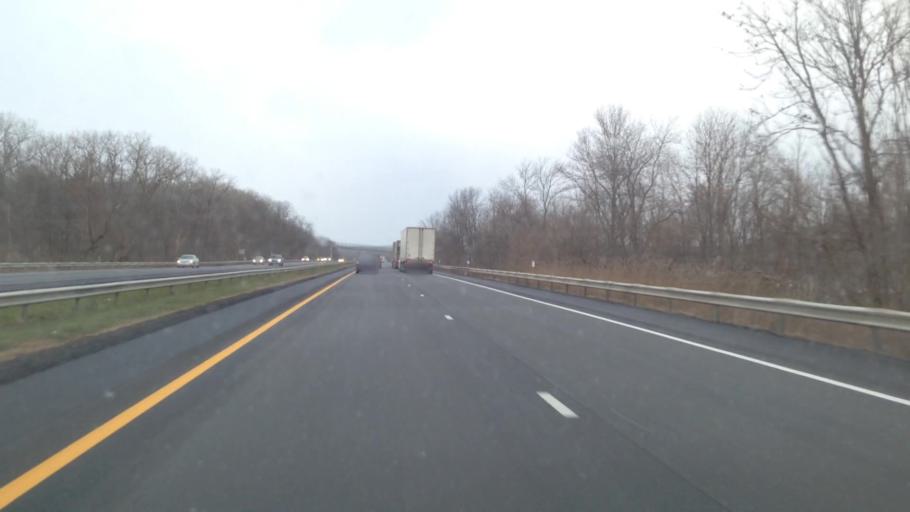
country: US
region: New York
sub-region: Montgomery County
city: Fonda
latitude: 42.9384
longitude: -74.3351
